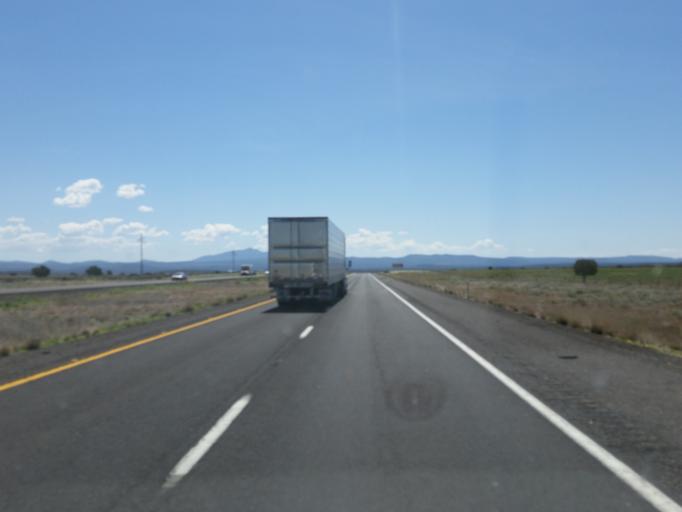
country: US
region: Arizona
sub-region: Yavapai County
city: Paulden
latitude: 35.2242
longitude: -112.5601
